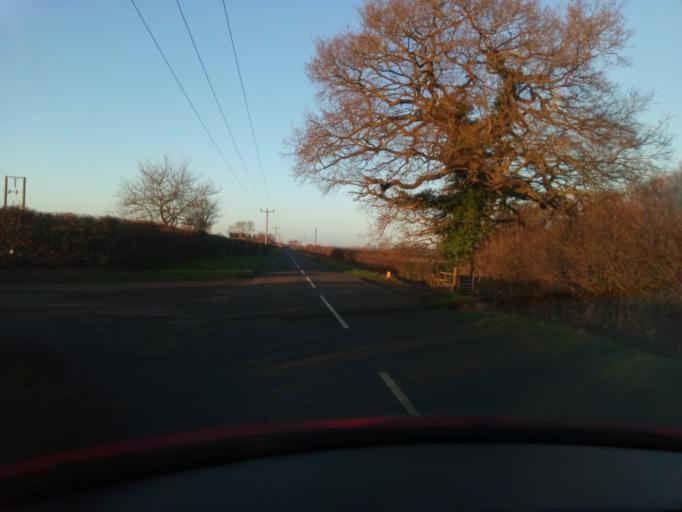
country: GB
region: England
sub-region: Leicestershire
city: Barrow upon Soar
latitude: 52.7731
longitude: -1.1466
